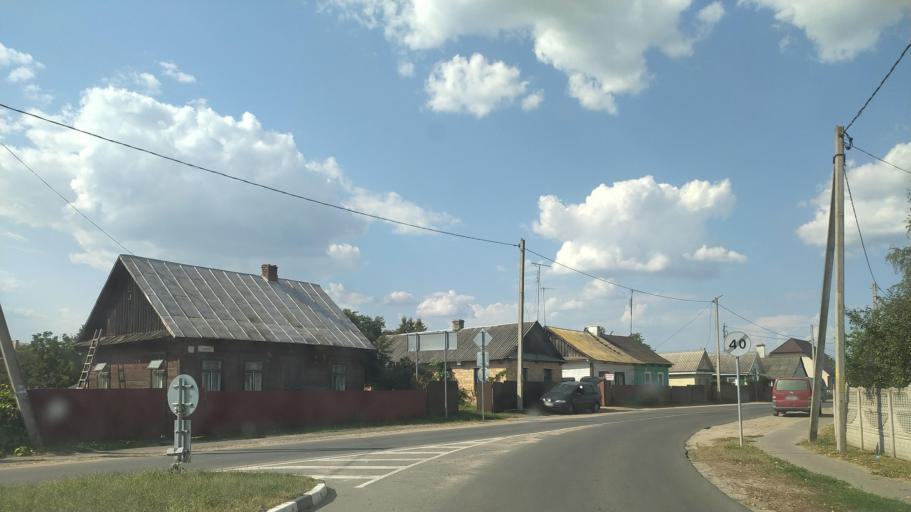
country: BY
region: Brest
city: Drahichyn
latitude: 52.1896
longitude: 25.1468
